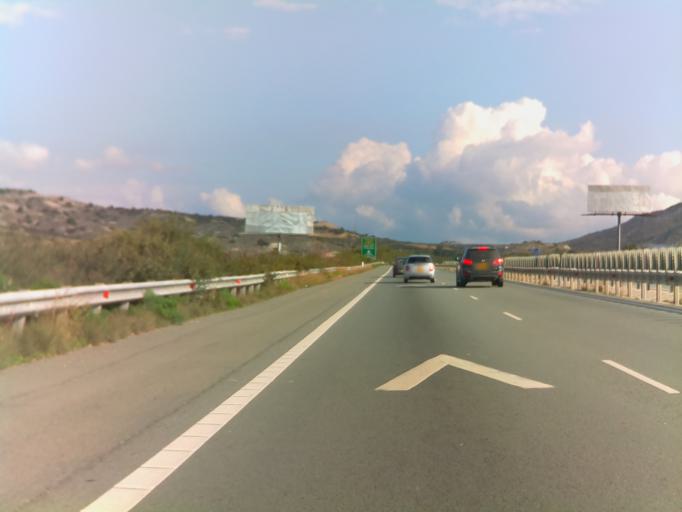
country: CY
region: Larnaka
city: Kofinou
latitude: 34.7714
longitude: 33.3365
